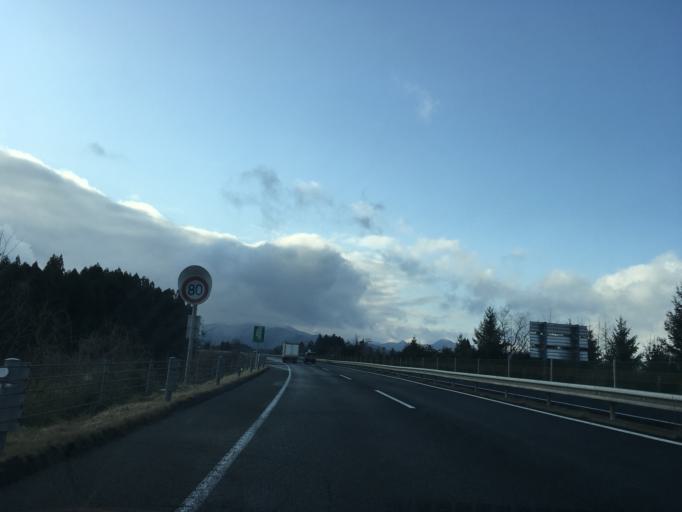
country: JP
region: Miyagi
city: Okawara
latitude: 38.1699
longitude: 140.6376
